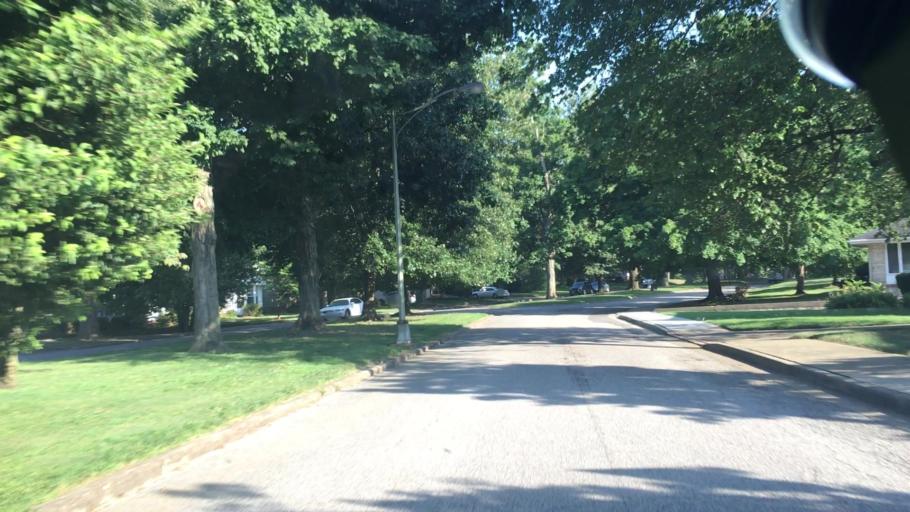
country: US
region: Indiana
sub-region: Vanderburgh County
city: Evansville
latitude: 37.9733
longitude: -87.5248
